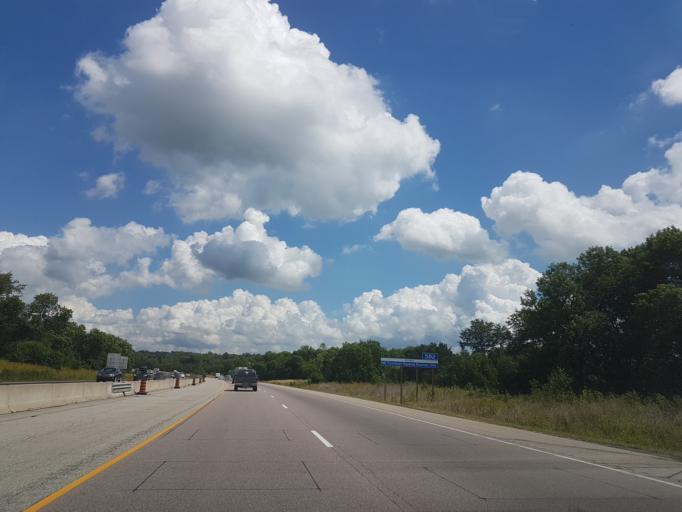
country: CA
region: Ontario
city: Skatepark
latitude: 44.2653
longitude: -76.9435
